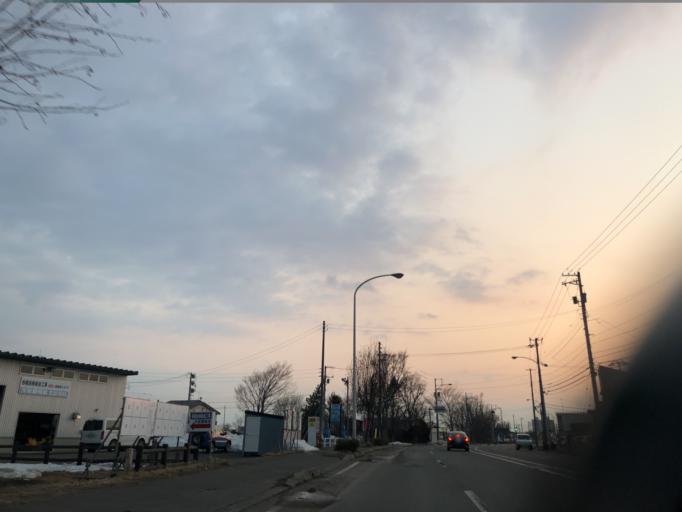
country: JP
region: Hokkaido
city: Chitose
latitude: 42.8311
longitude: 141.6883
